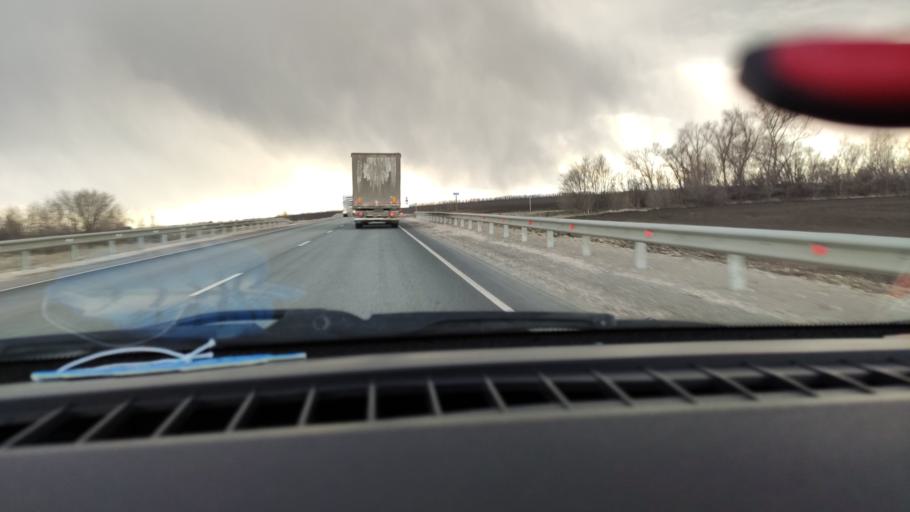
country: RU
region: Saratov
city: Yelshanka
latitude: 51.8445
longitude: 46.4816
